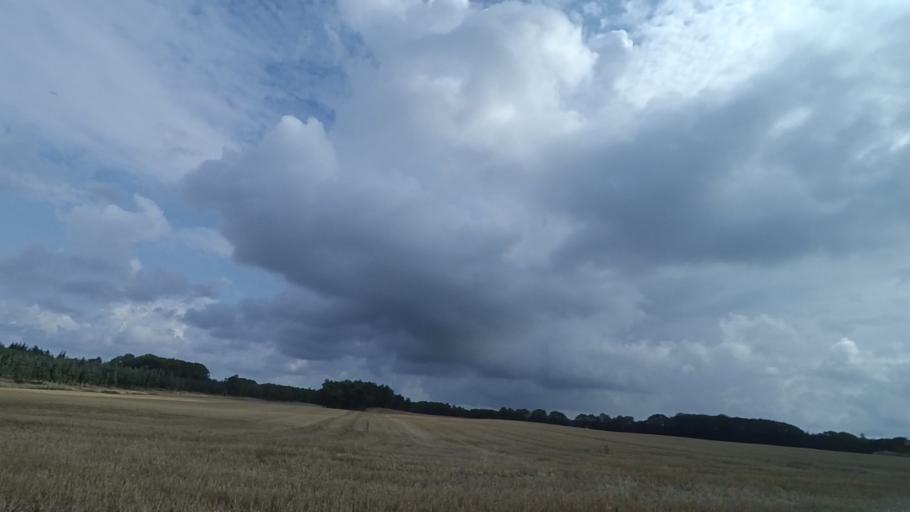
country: DK
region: Central Jutland
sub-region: Syddjurs Kommune
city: Ryomgard
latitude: 56.4506
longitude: 10.5542
